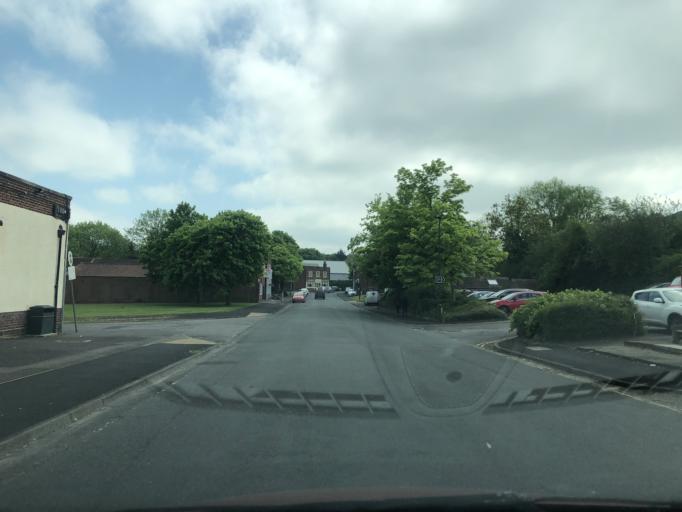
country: GB
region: England
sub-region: North Yorkshire
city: Catterick Garrison
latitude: 54.3768
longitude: -1.7209
